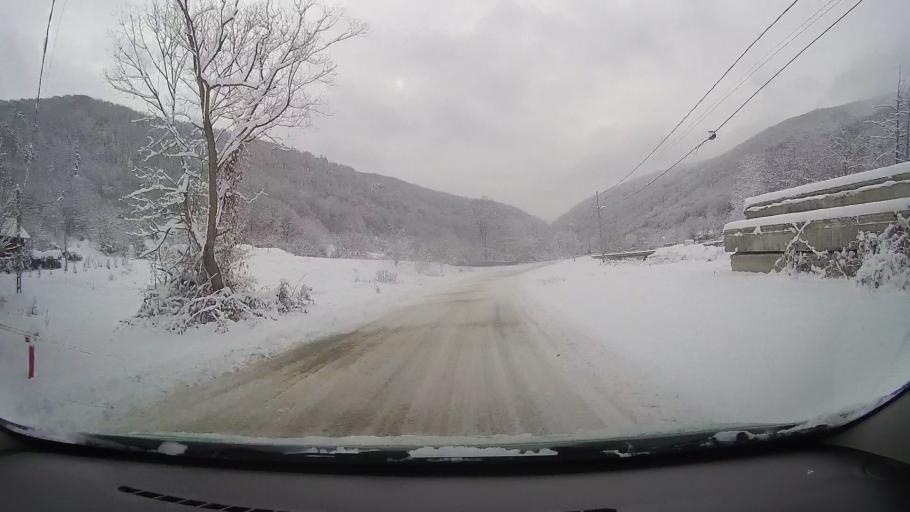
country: RO
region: Alba
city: Pianu de Sus
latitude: 45.8825
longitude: 23.4918
